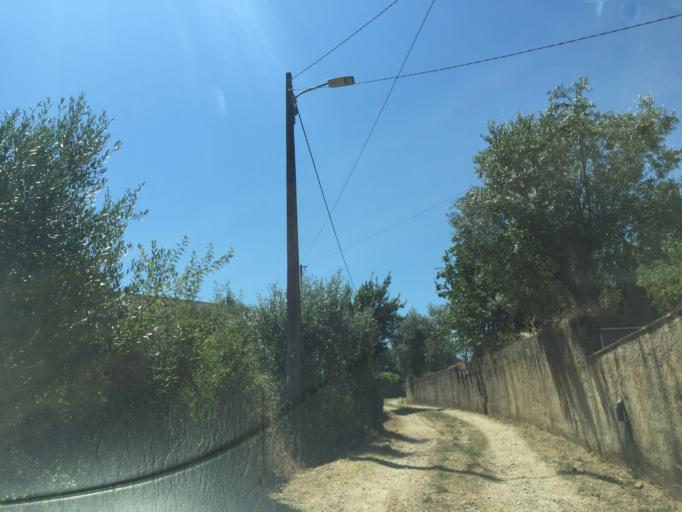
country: PT
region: Santarem
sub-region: Ferreira do Zezere
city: Ferreira do Zezere
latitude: 39.6241
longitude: -8.3183
